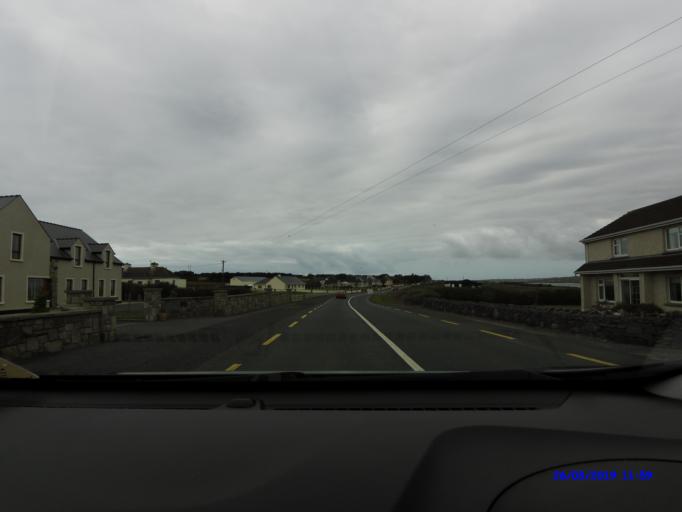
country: IE
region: Connaught
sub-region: Maigh Eo
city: Belmullet
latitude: 54.2092
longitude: -9.9437
